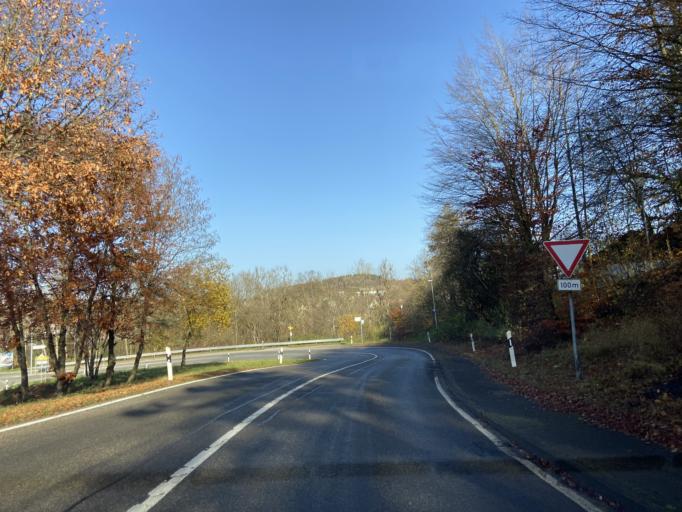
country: DE
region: Baden-Wuerttemberg
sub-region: Tuebingen Region
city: Sigmaringendorf
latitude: 48.0620
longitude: 9.2622
